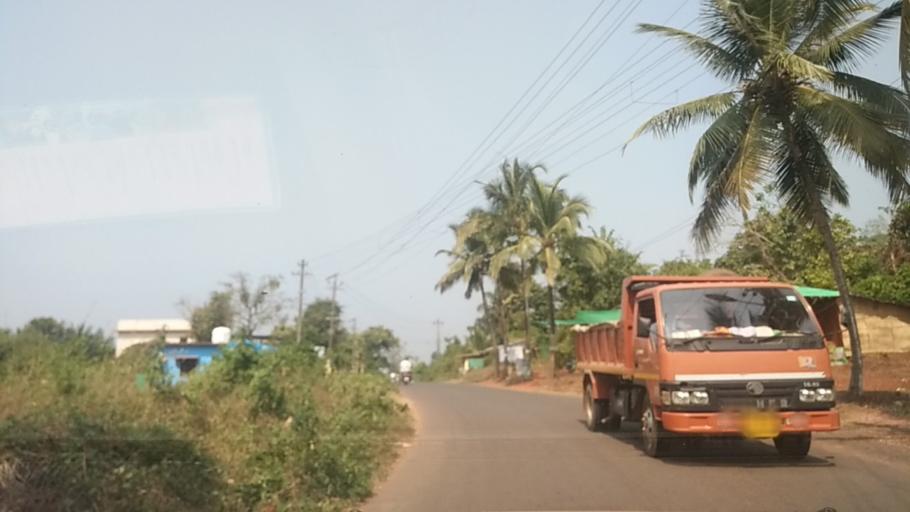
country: IN
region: Goa
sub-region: North Goa
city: Arambol
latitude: 15.6776
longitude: 73.7111
